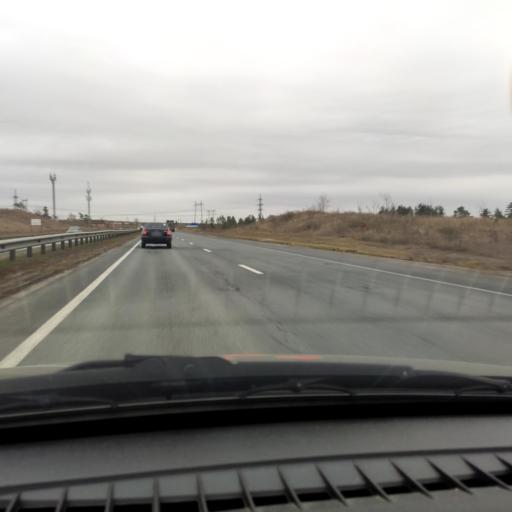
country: RU
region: Samara
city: Zhigulevsk
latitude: 53.5239
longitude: 49.5274
